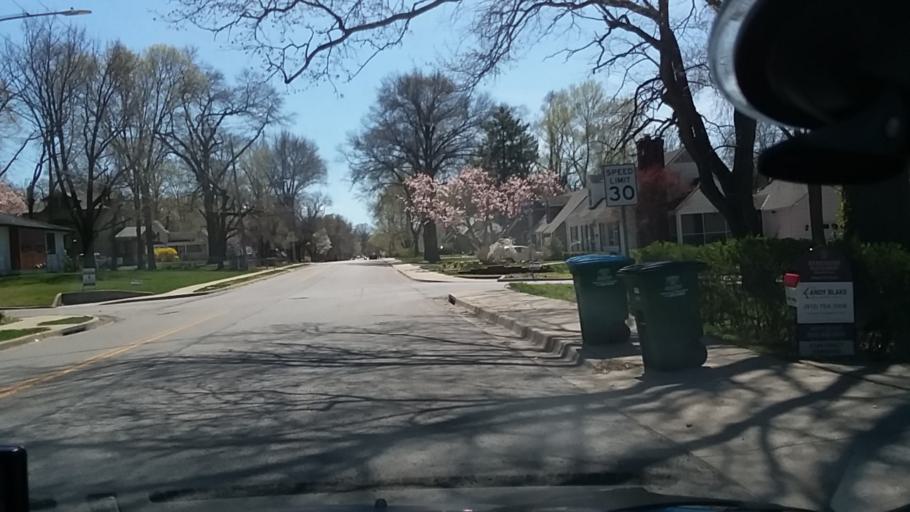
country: US
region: Kansas
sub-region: Johnson County
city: Westwood
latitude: 39.0386
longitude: -94.6213
